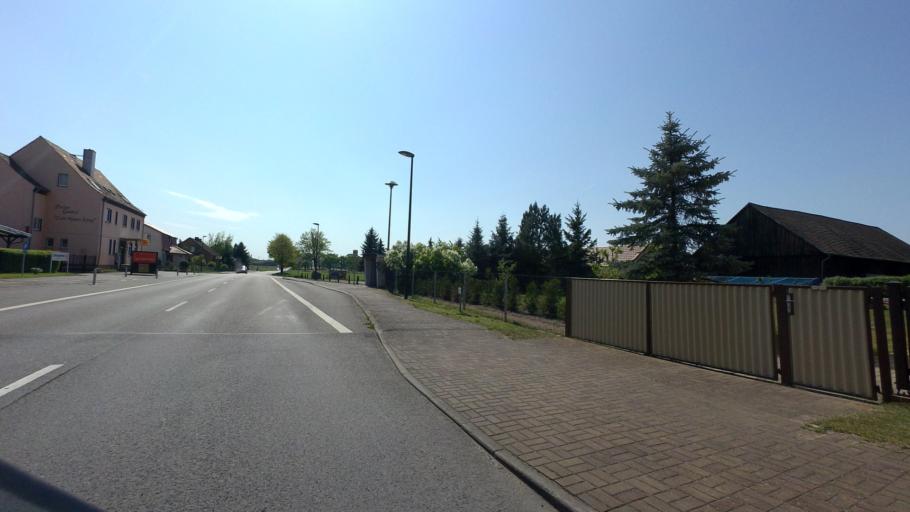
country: DE
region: Brandenburg
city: Neu Zauche
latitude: 52.0288
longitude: 14.0906
